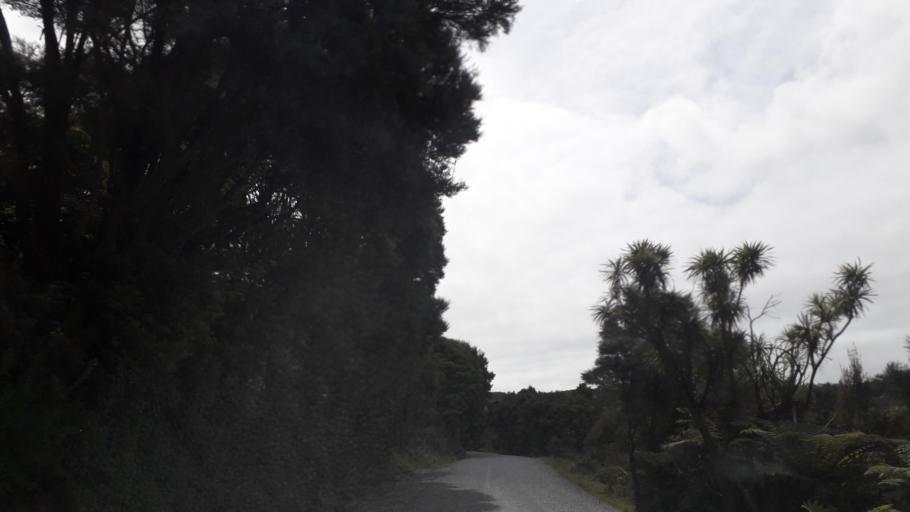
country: NZ
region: Northland
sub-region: Far North District
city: Taipa
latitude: -35.0320
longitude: 173.5627
